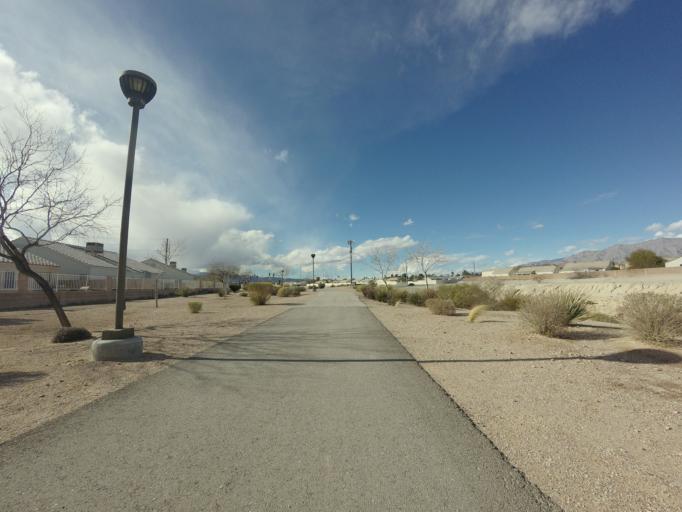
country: US
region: Nevada
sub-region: Clark County
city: North Las Vegas
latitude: 36.2566
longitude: -115.1698
